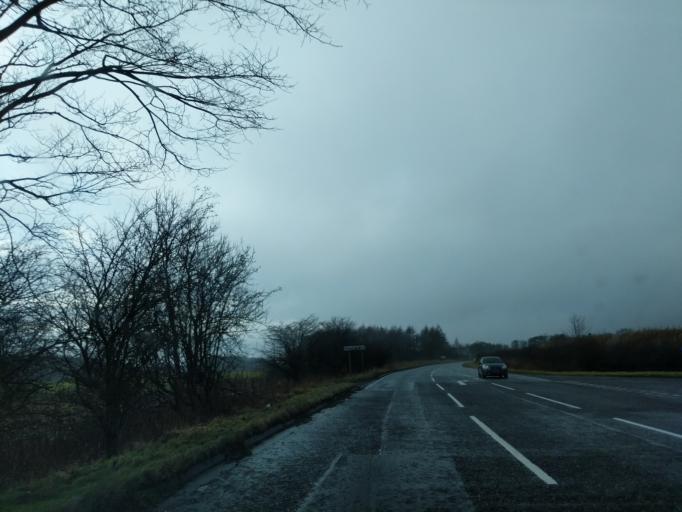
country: GB
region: Scotland
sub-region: Perth and Kinross
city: Kinross
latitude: 56.2048
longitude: -3.4694
